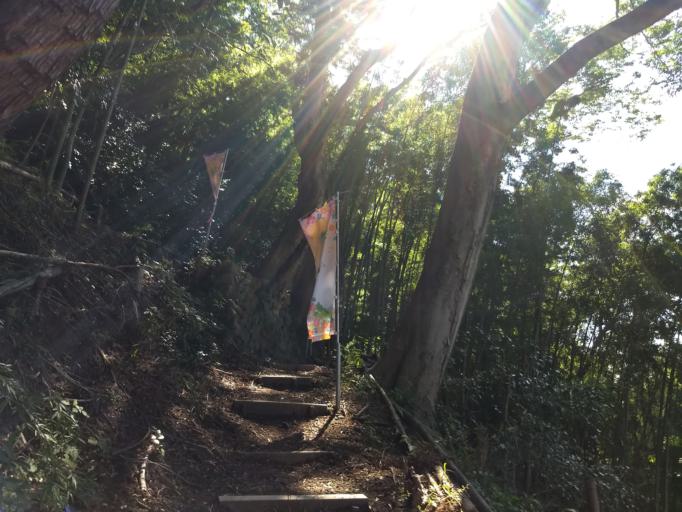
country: JP
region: Gunma
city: Annaka
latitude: 36.3385
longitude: 138.7328
